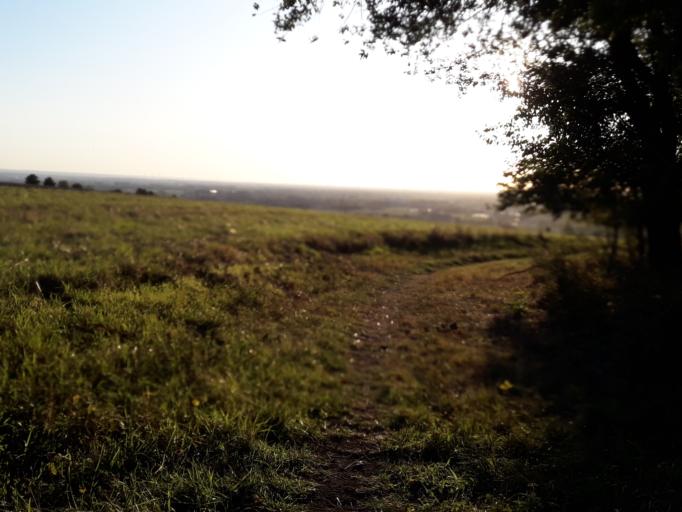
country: DE
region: North Rhine-Westphalia
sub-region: Regierungsbezirk Detmold
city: Schlangen
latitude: 51.7913
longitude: 8.8703
